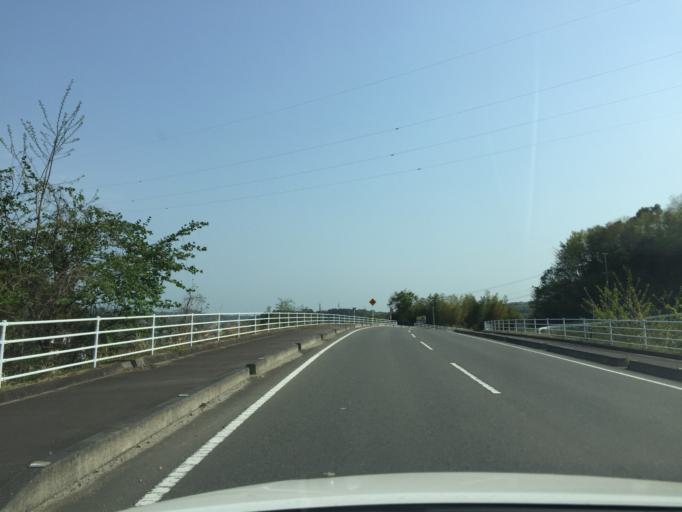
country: JP
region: Fukushima
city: Iwaki
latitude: 37.1387
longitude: 140.8544
